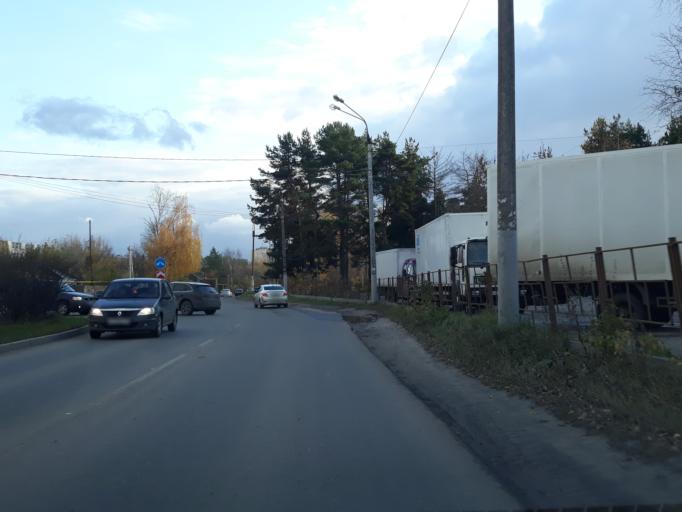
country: RU
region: Nizjnij Novgorod
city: Neklyudovo
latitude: 56.3389
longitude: 43.8665
